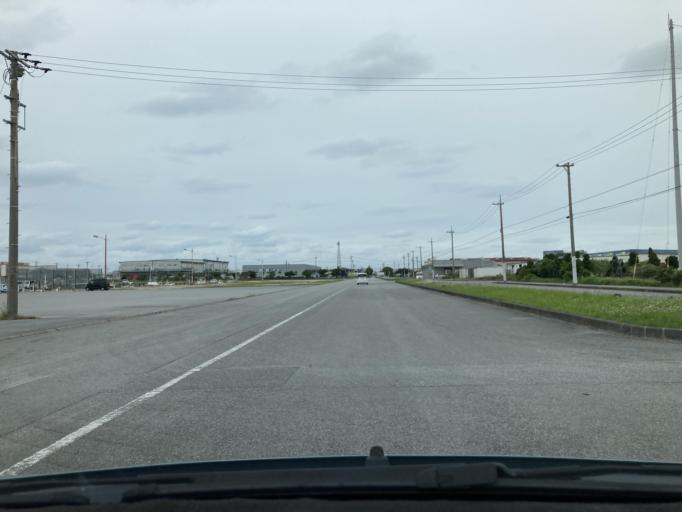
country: JP
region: Okinawa
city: Itoman
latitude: 26.1346
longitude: 127.6616
